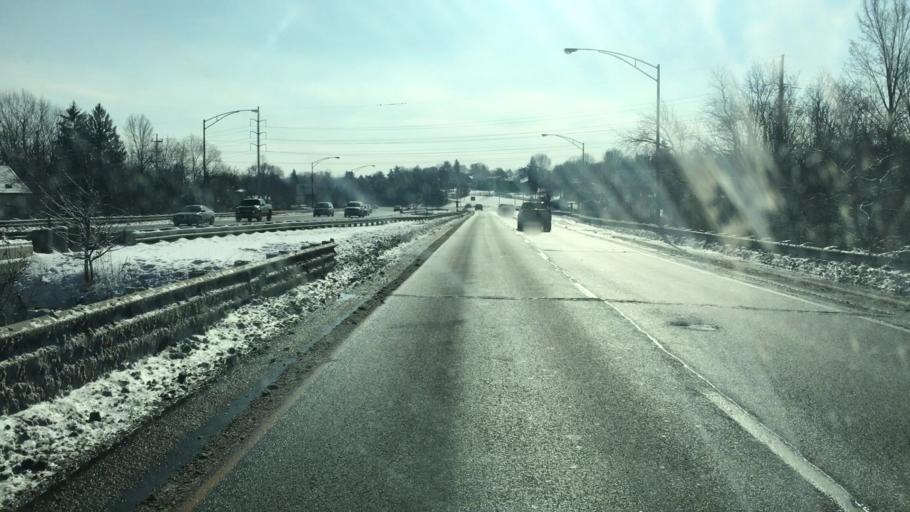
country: US
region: Ohio
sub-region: Trumbull County
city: Girard
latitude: 41.1138
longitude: -80.6922
